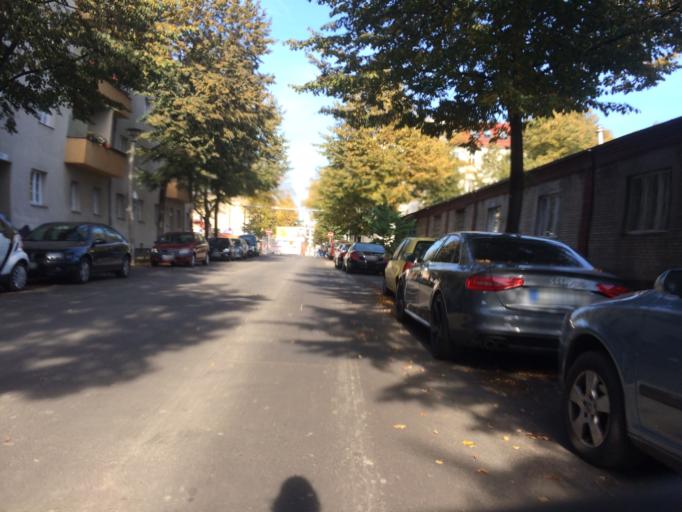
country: DE
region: Berlin
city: Prenzlauer Berg Bezirk
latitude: 52.5513
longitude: 13.4360
